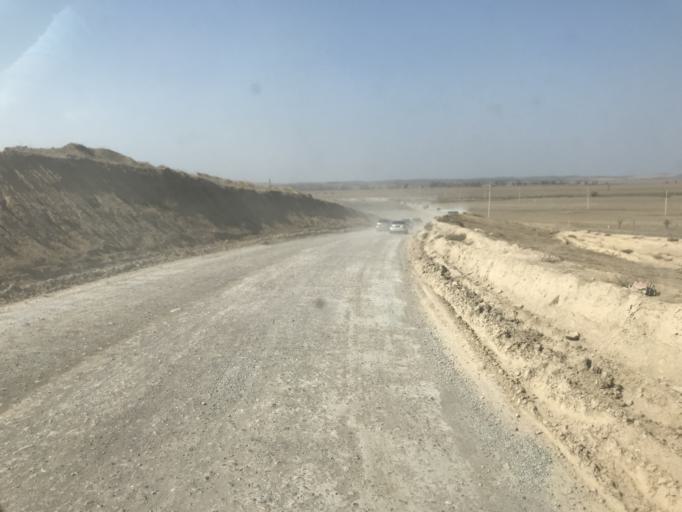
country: KG
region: Chuy
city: Bystrovka
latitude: 43.3219
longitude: 76.0438
